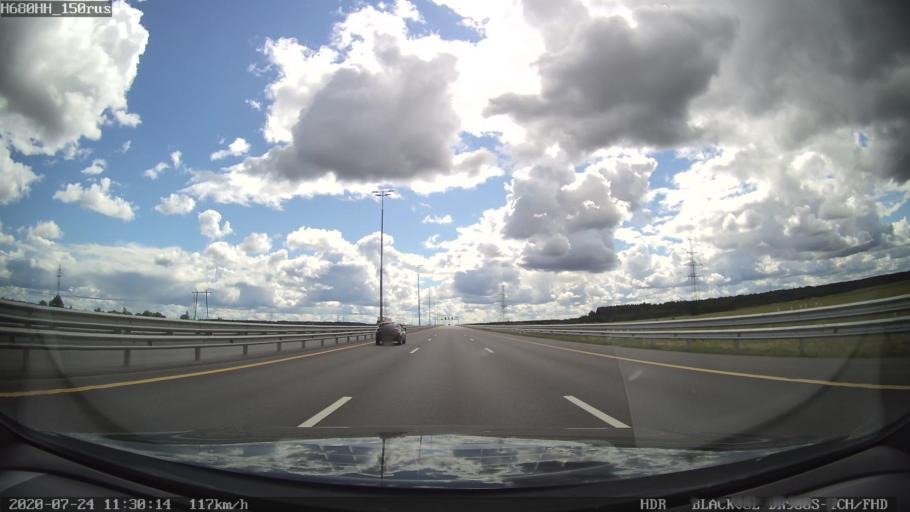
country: RU
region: Leningrad
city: Krasnyy Bor
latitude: 59.6716
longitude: 30.6086
